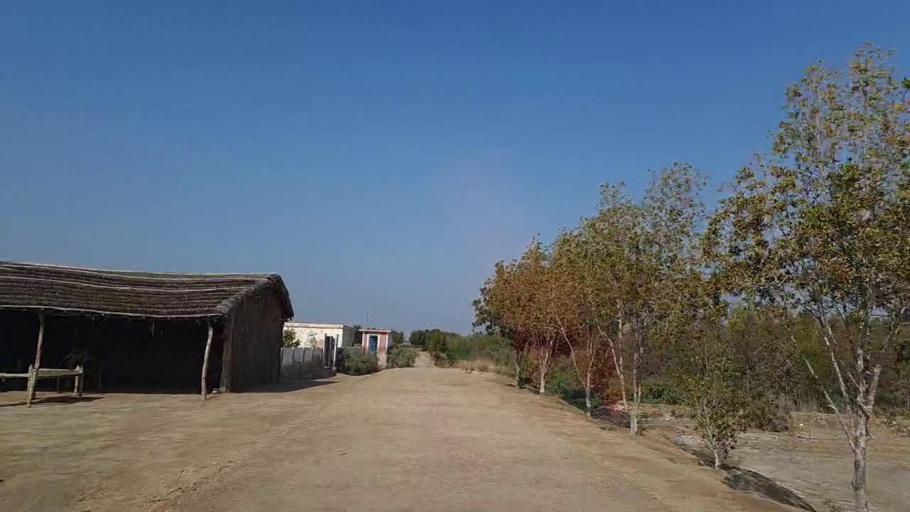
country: PK
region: Sindh
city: Tando Mittha Khan
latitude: 26.0280
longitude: 69.1069
